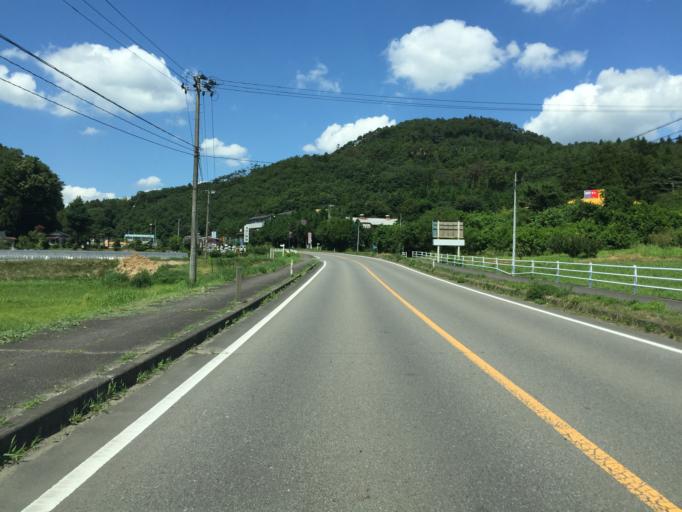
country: JP
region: Fukushima
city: Nihommatsu
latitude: 37.6357
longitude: 140.4645
